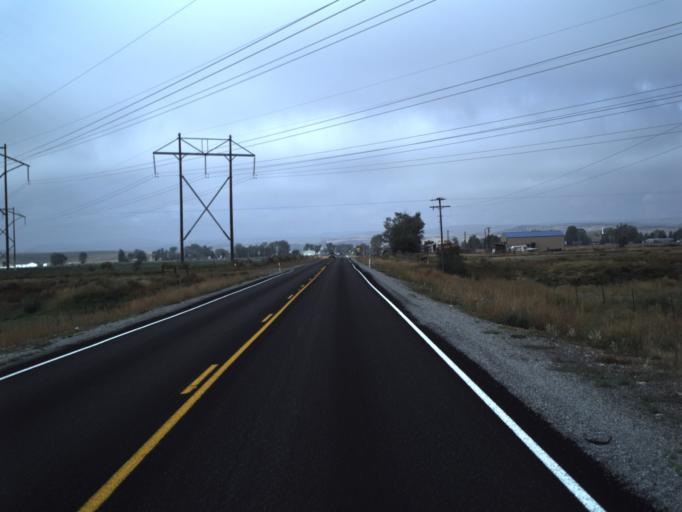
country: US
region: Utah
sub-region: Rich County
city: Randolph
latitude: 41.5174
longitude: -111.1499
